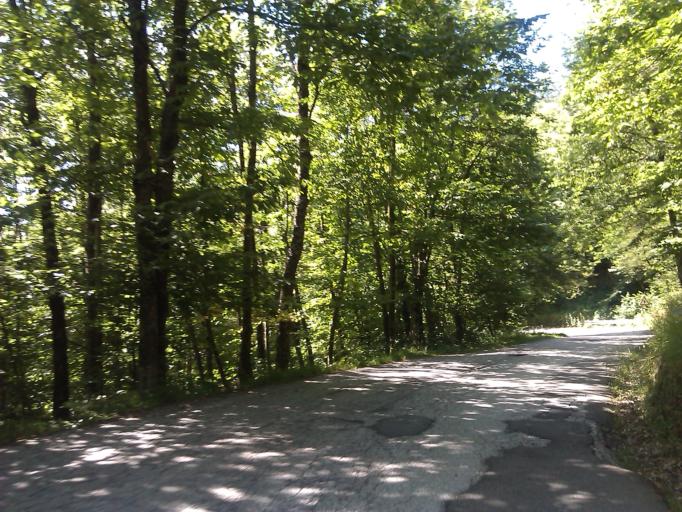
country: IT
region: Tuscany
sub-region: Provincia di Pistoia
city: Sambuca Pistoiese
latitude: 44.0944
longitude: 11.0450
